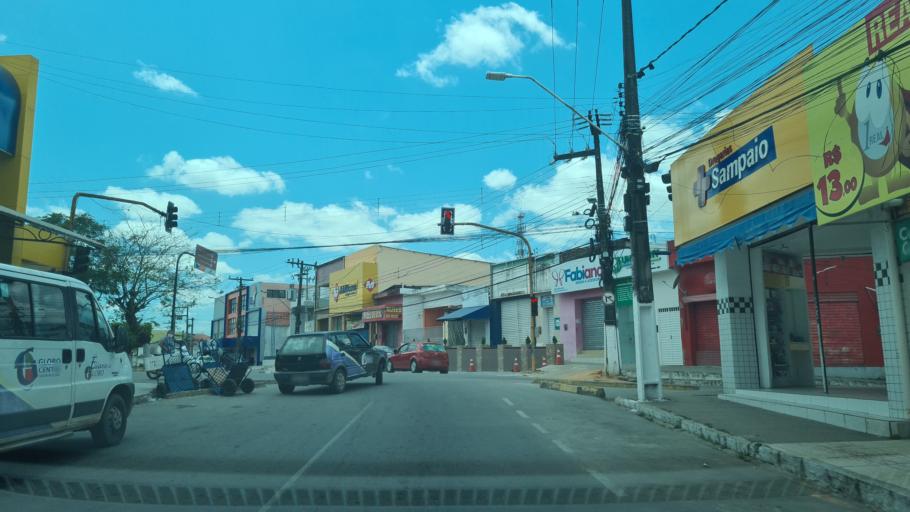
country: BR
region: Alagoas
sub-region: Uniao Dos Palmares
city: Uniao dos Palmares
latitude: -9.1577
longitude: -36.0323
